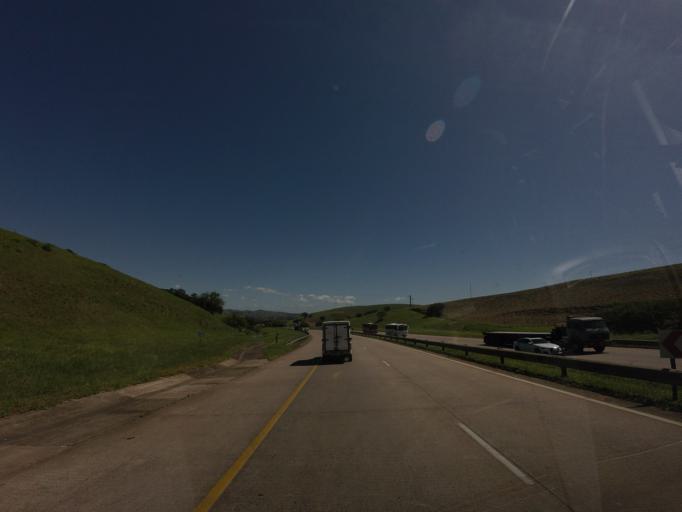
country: ZA
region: KwaZulu-Natal
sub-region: iLembe District Municipality
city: Stanger
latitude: -29.3841
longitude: 31.2971
